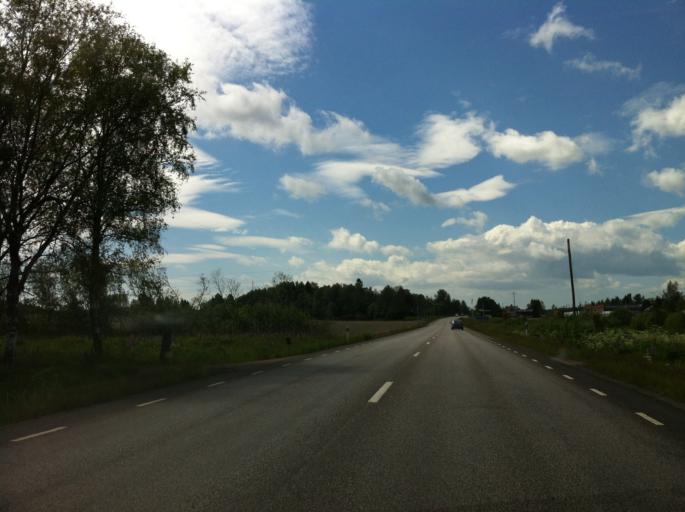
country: SE
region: Vaermland
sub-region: Saffle Kommun
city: Saeffle
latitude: 59.1925
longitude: 13.0208
